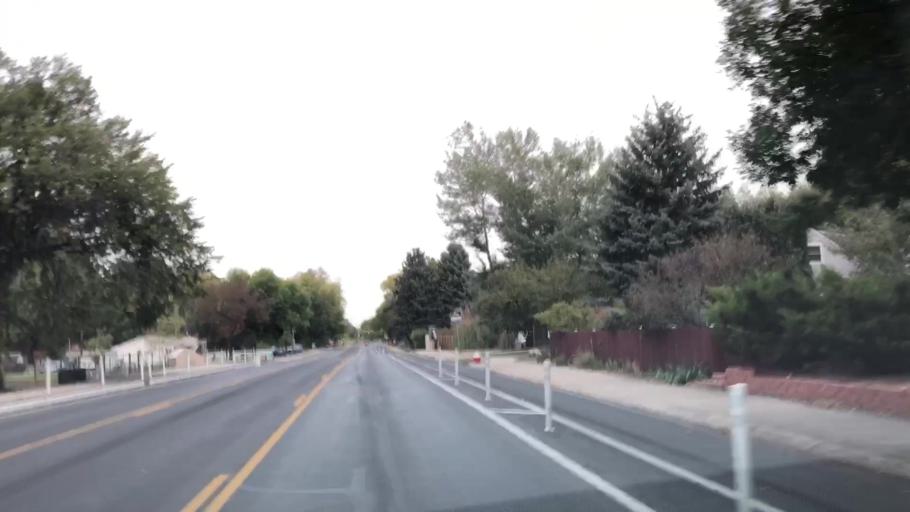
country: US
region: Colorado
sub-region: Larimer County
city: Fort Collins
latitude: 40.5819
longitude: -105.1111
